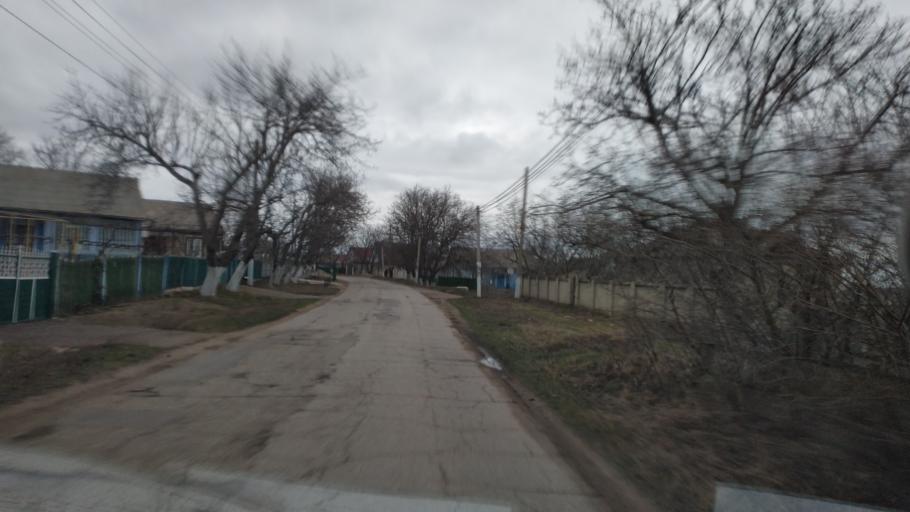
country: MD
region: Bender
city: Bender
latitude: 46.7730
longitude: 29.4834
